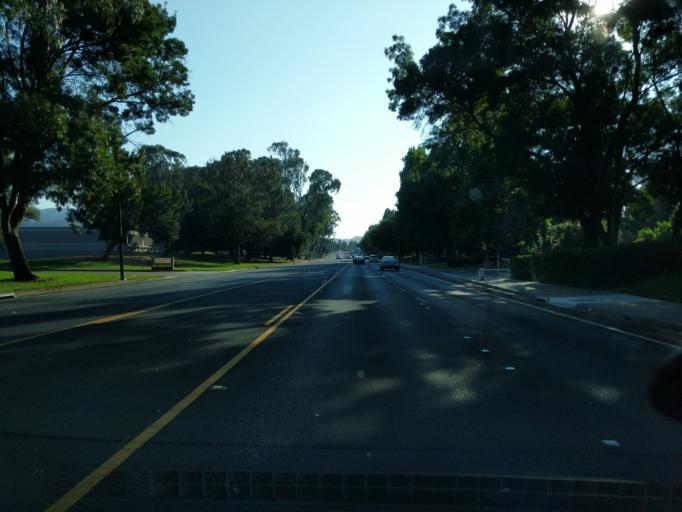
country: US
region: California
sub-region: Contra Costa County
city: San Ramon
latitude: 37.7737
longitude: -121.9670
